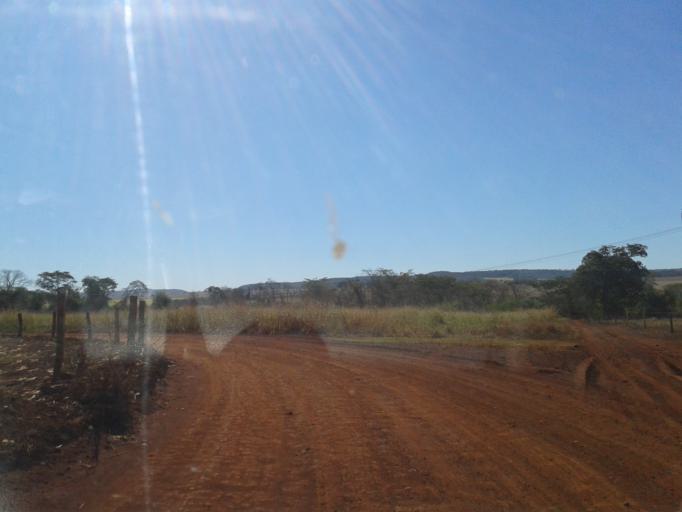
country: BR
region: Minas Gerais
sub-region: Centralina
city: Centralina
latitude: -18.5840
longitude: -49.1303
